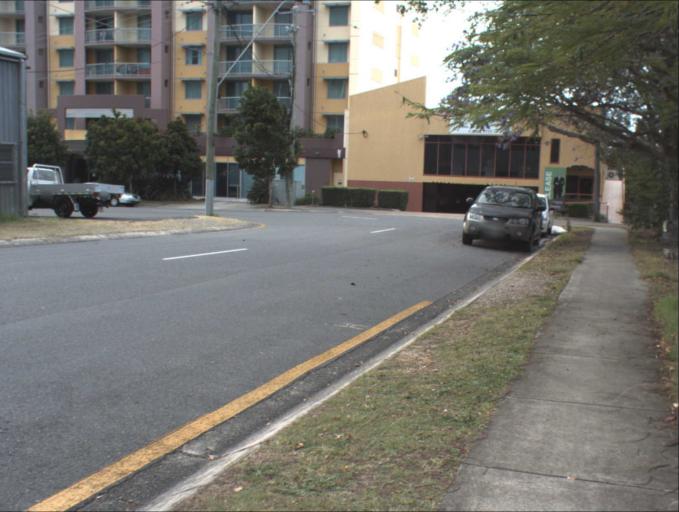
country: AU
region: Queensland
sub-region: Logan
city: Springwood
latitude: -27.6168
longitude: 153.1278
